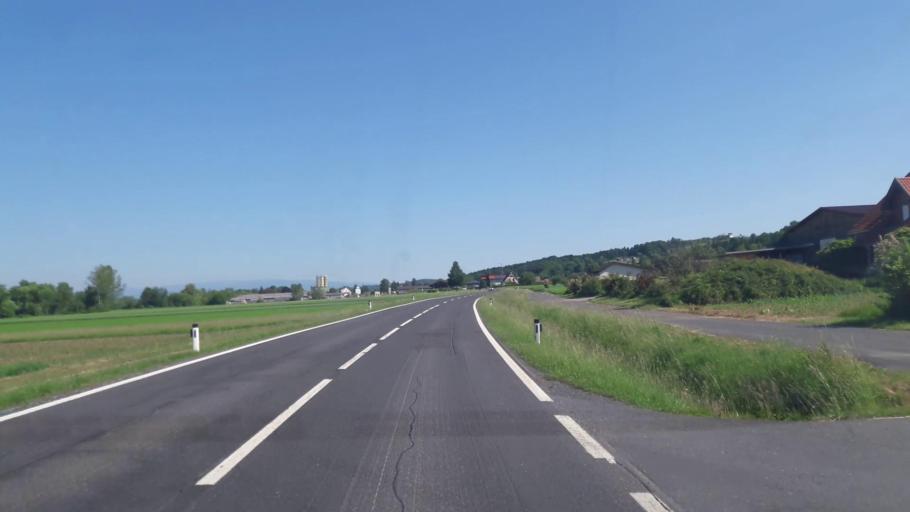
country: AT
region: Styria
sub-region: Politischer Bezirk Hartberg-Fuerstenfeld
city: Burgau
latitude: 47.1445
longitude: 16.1176
